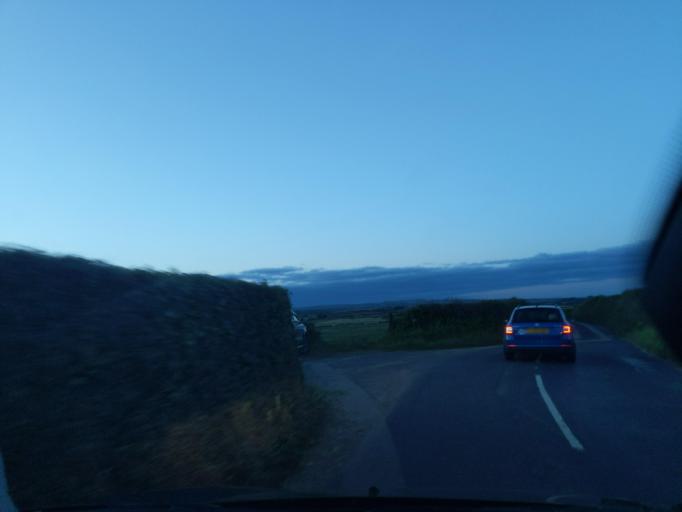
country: GB
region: England
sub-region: Cornwall
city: St. Buryan
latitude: 50.0867
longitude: -5.6034
